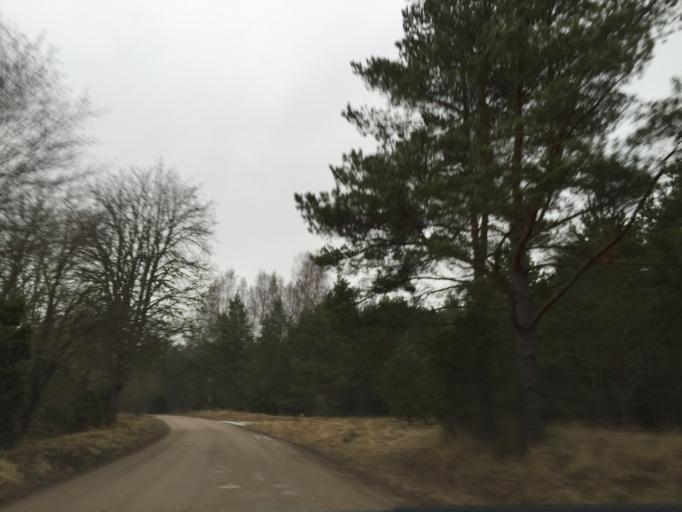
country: EE
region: Saare
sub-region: Kuressaare linn
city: Kuressaare
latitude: 58.4504
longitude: 22.2462
